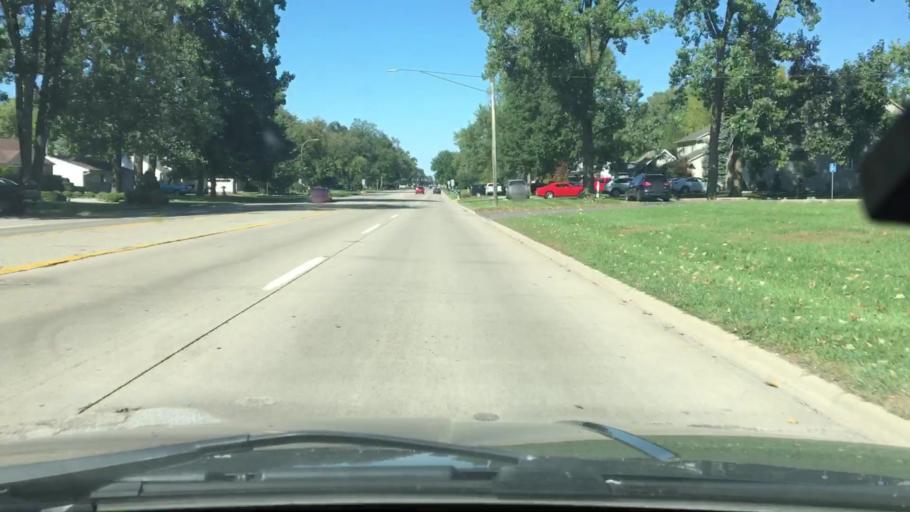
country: US
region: Michigan
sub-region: Wayne County
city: Livonia
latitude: 42.3910
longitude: -83.3536
